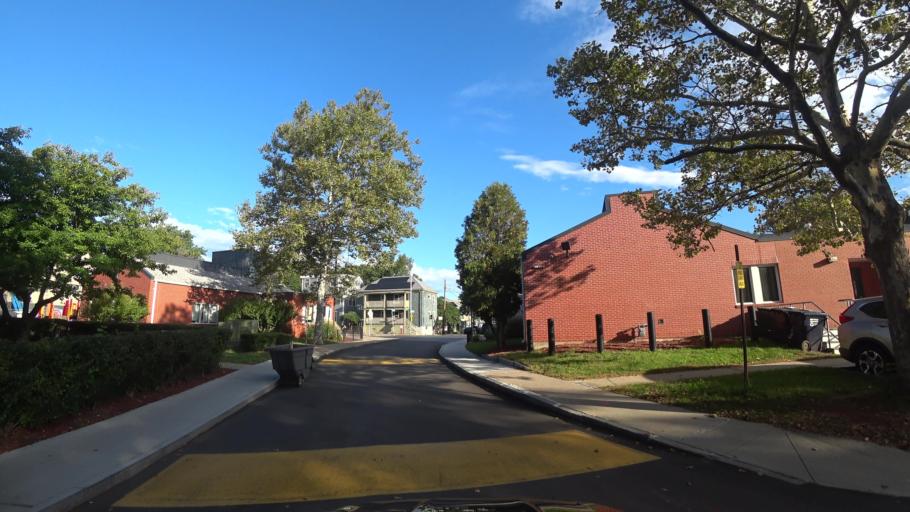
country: US
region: Massachusetts
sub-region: Middlesex County
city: Arlington
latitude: 42.3932
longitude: -71.1350
